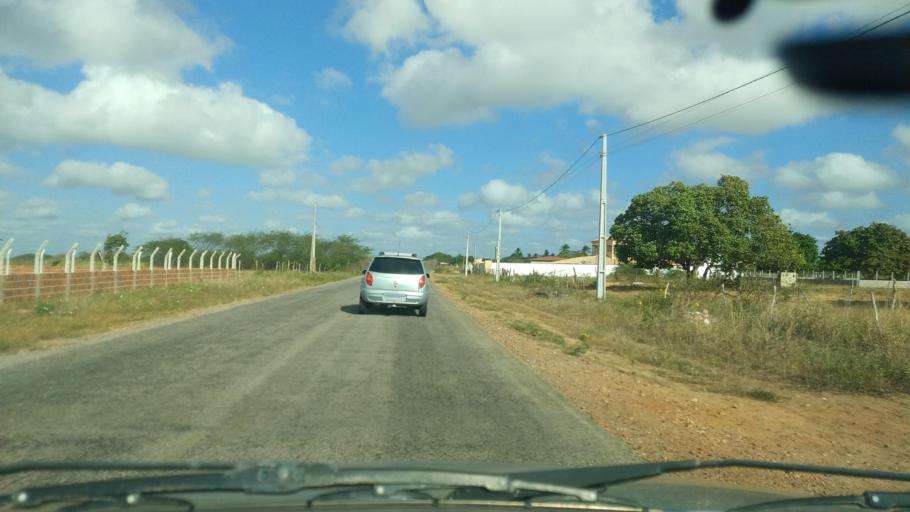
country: BR
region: Rio Grande do Norte
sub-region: Sao Paulo Do Potengi
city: Sao Paulo do Potengi
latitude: -5.9162
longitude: -35.7203
